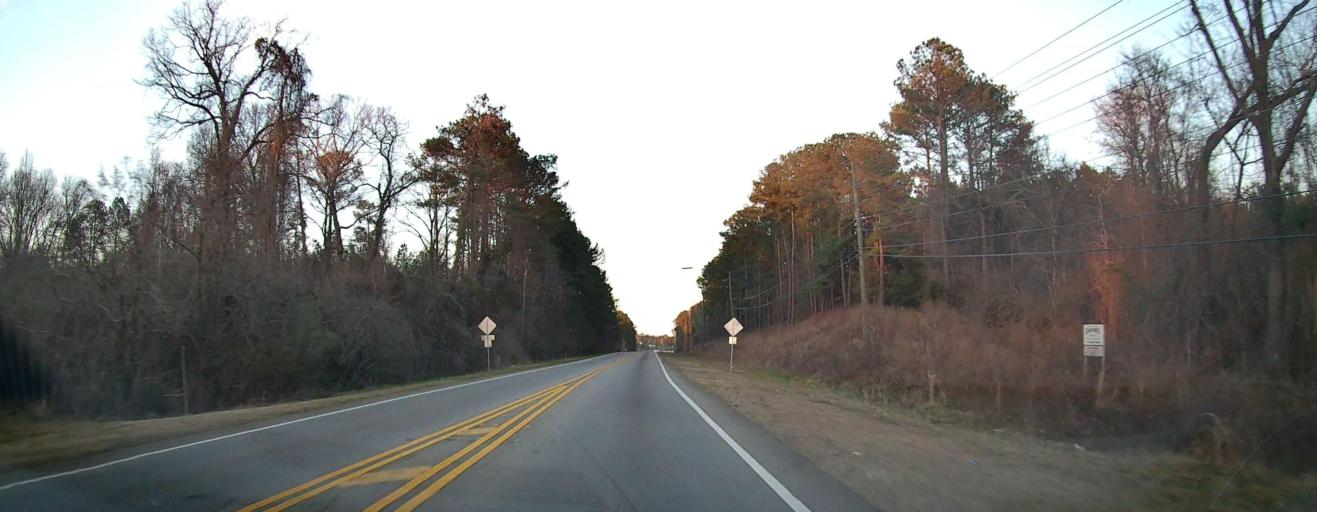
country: US
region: Georgia
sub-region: Troup County
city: La Grange
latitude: 33.0227
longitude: -84.9931
